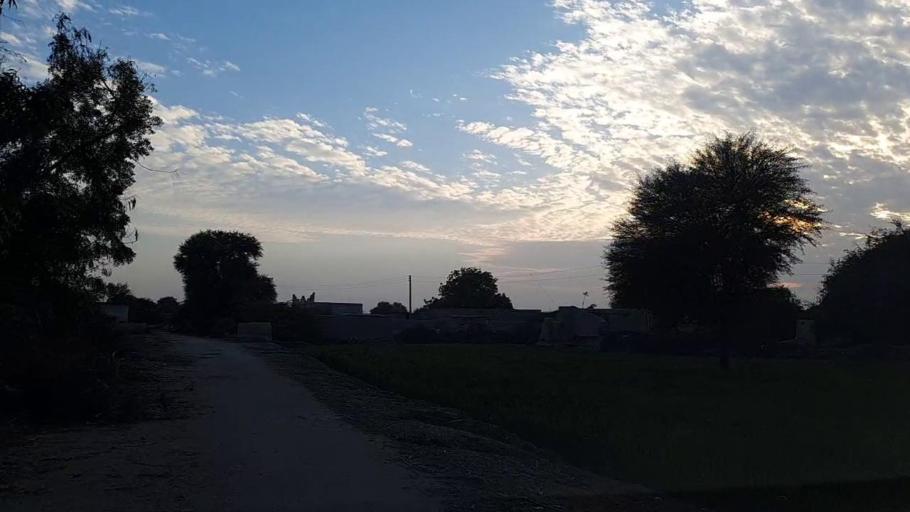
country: PK
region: Sindh
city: Daur
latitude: 26.4135
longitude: 68.4775
